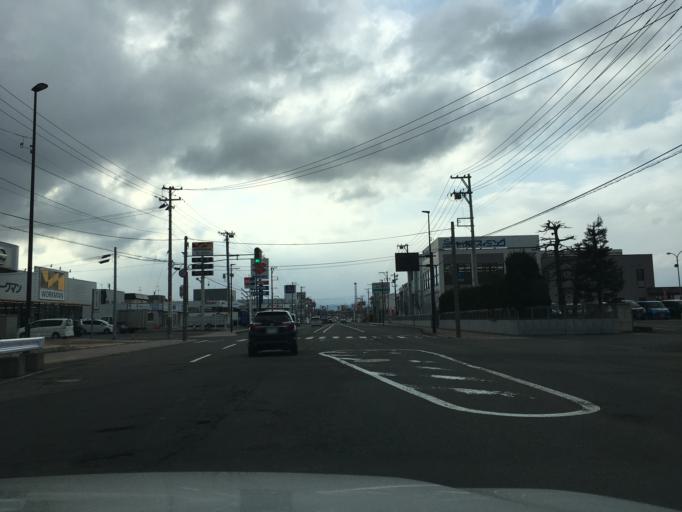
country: JP
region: Aomori
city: Aomori Shi
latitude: 40.8256
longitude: 140.7117
